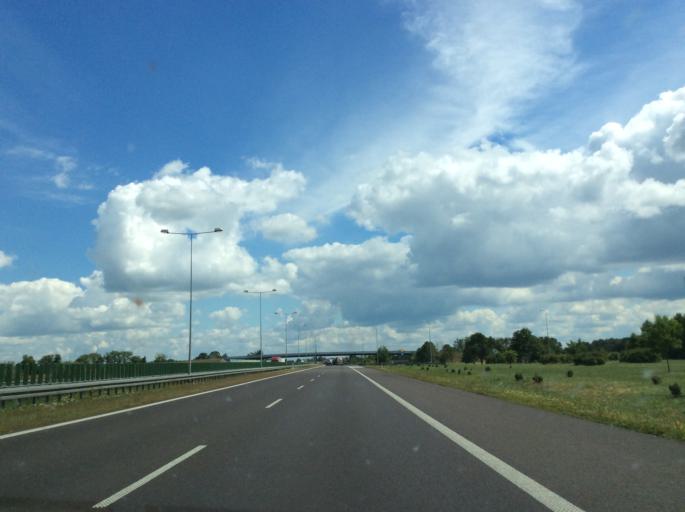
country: PL
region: Greater Poland Voivodeship
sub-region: Powiat turecki
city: Brudzew
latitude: 52.1344
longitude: 18.6362
